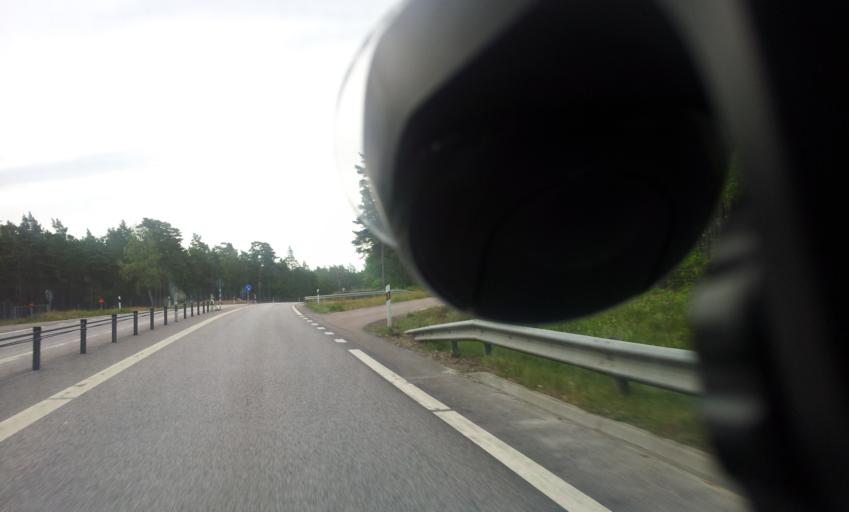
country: SE
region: Kalmar
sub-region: Oskarshamns Kommun
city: Paskallavik
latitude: 57.1253
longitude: 16.4861
